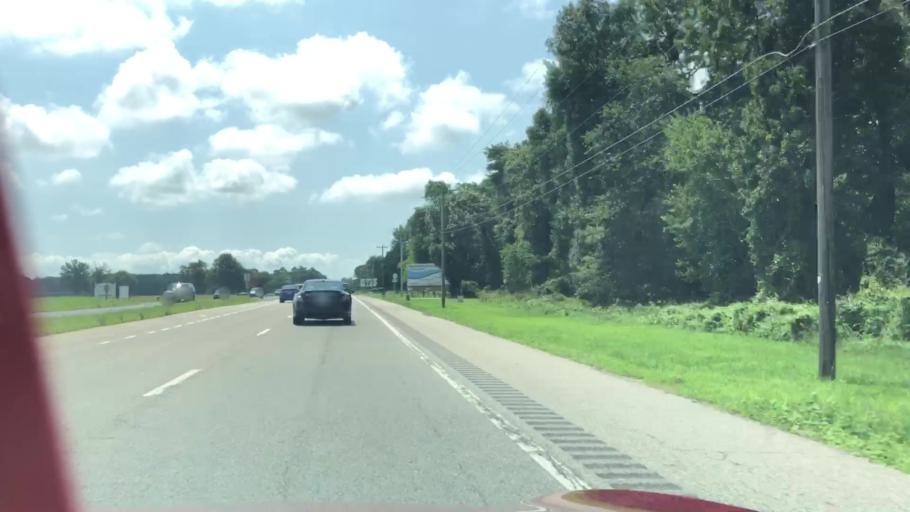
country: US
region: Virginia
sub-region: Northampton County
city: Cape Charles
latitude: 37.2429
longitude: -75.9717
